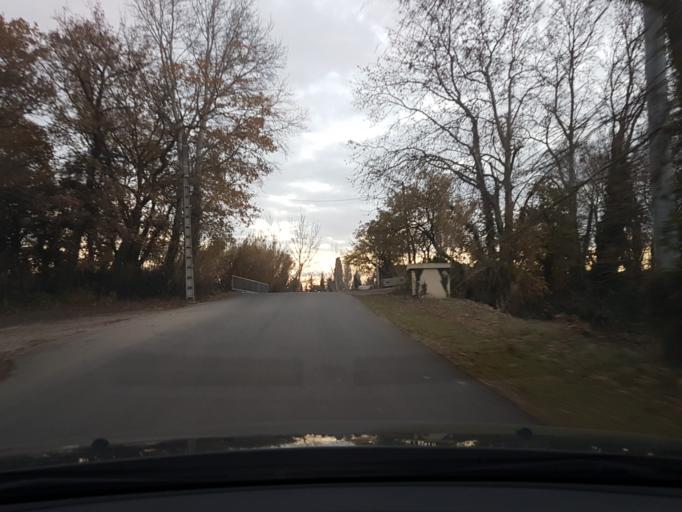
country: FR
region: Provence-Alpes-Cote d'Azur
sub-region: Departement du Vaucluse
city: Loriol-du-Comtat
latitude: 44.0806
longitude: 4.9981
